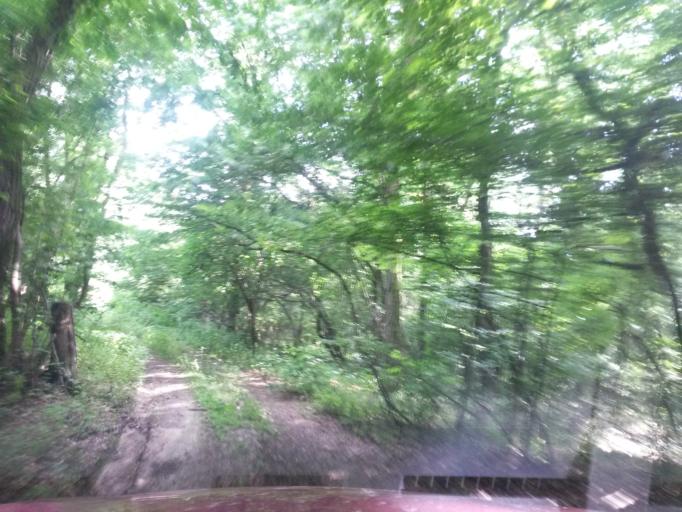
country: SK
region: Kosicky
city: Moldava nad Bodvou
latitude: 48.6234
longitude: 21.0992
